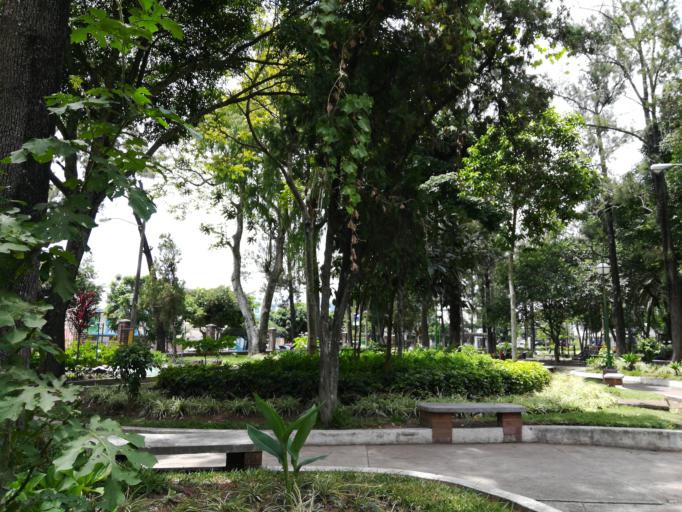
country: GT
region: Guatemala
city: Guatemala City
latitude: 14.6514
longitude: -90.5127
